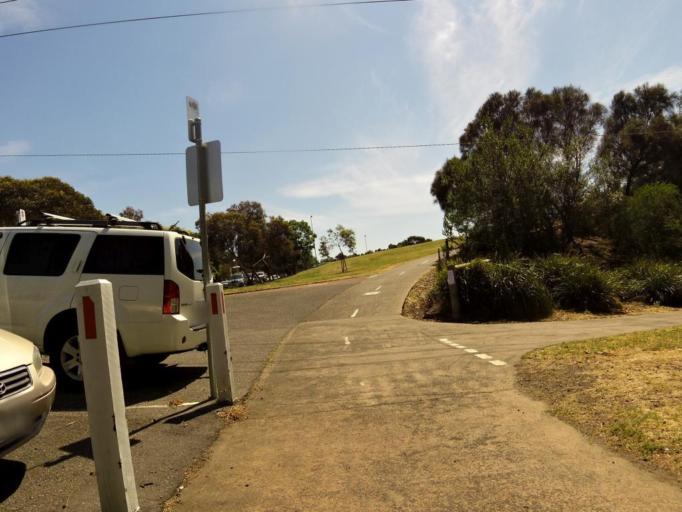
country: AU
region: Victoria
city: Abbotsford
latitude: -37.7935
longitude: 145.0023
